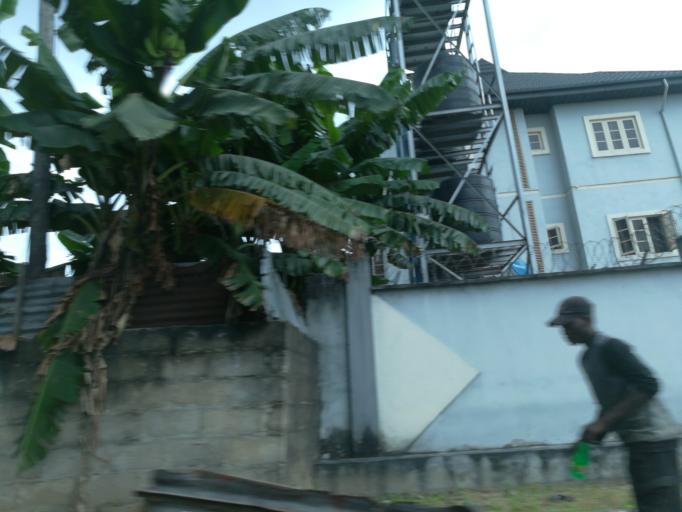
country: NG
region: Rivers
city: Port Harcourt
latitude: 4.8224
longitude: 7.0675
